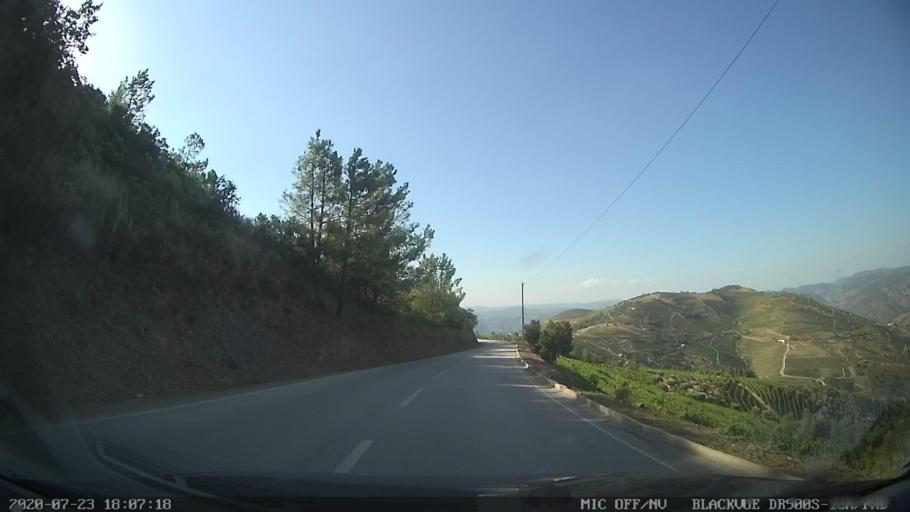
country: PT
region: Viseu
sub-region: Sao Joao da Pesqueira
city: Sao Joao da Pesqueira
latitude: 41.1672
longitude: -7.4352
